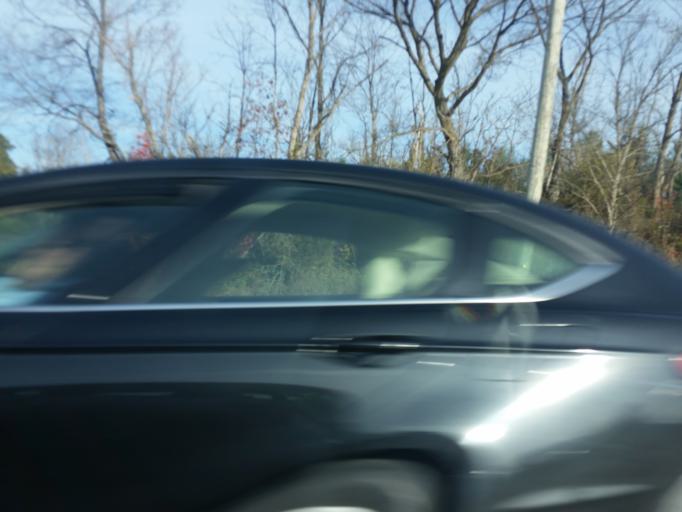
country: US
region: Kentucky
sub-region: Pendleton County
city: Falmouth
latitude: 38.7971
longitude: -84.3550
